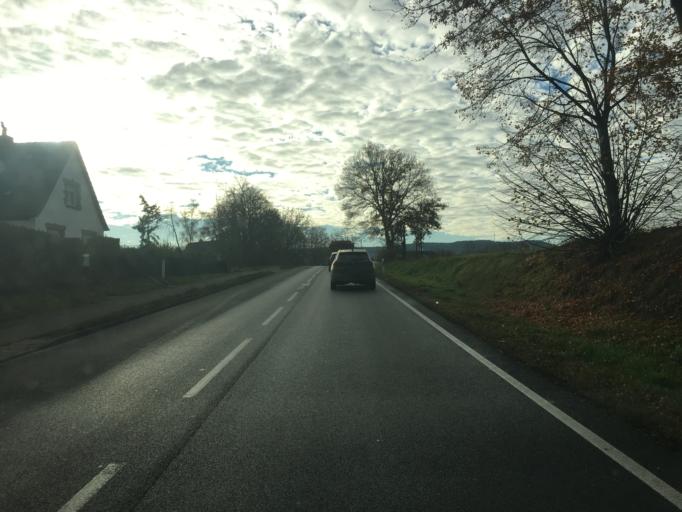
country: DE
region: North Rhine-Westphalia
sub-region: Regierungsbezirk Koln
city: Mechernich
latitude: 50.5943
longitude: 6.6304
